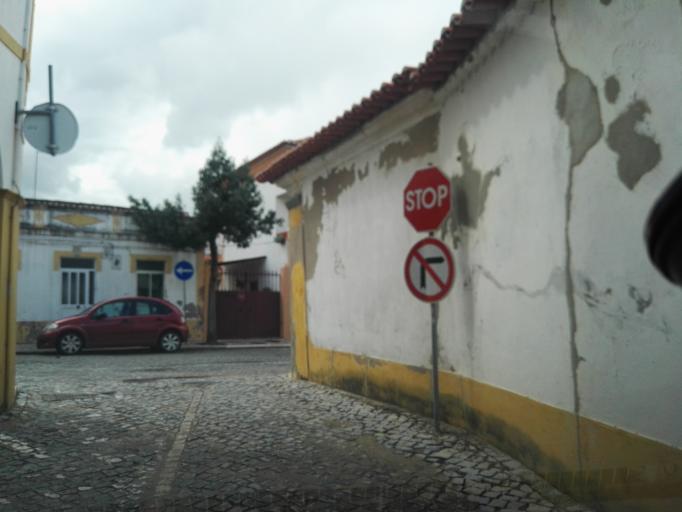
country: PT
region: Santarem
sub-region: Golega
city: Golega
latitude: 39.4048
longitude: -8.4861
